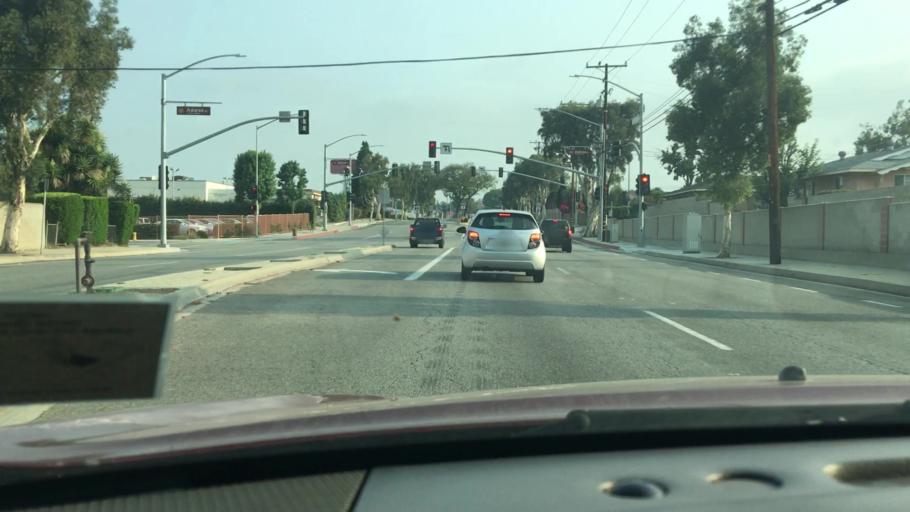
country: US
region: California
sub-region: Los Angeles County
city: La Mirada
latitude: 33.9136
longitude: -118.0293
